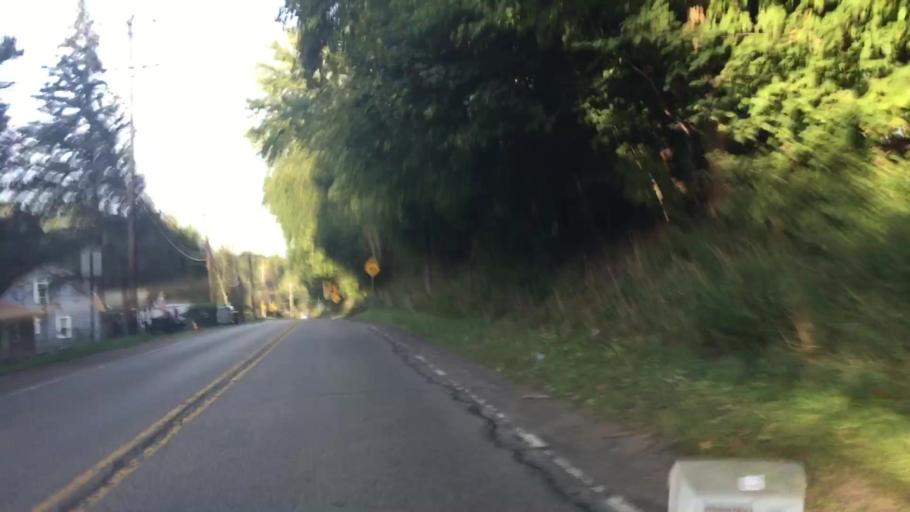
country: US
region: Pennsylvania
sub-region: Beaver County
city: Ambridge
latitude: 40.5667
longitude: -80.2662
